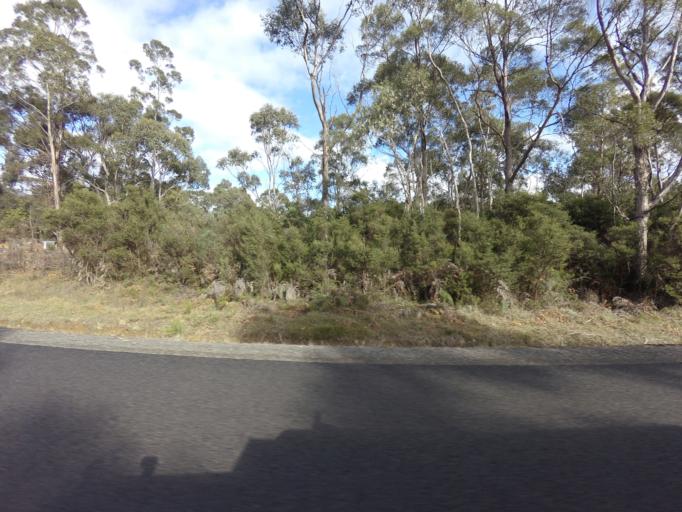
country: AU
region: Tasmania
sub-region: Huon Valley
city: Geeveston
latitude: -43.4390
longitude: 146.9042
